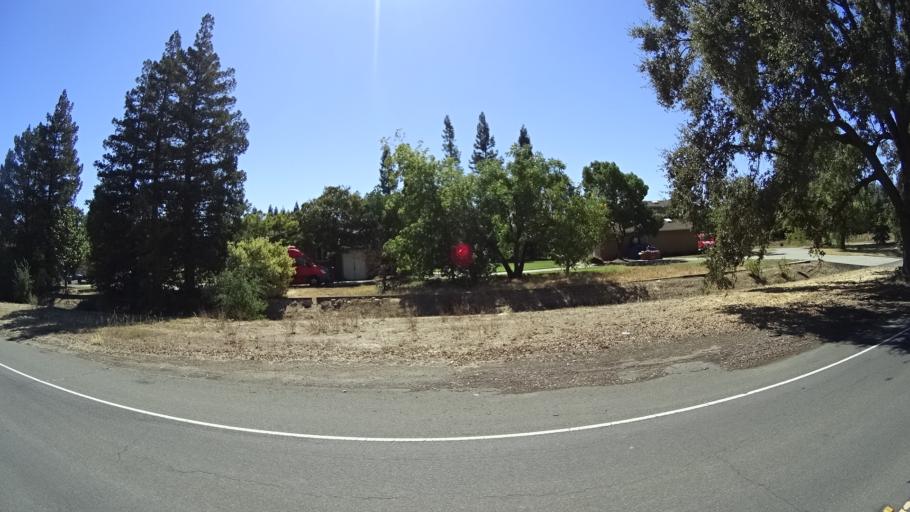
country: US
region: California
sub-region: Sacramento County
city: Vineyard
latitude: 38.4382
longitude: -121.3197
